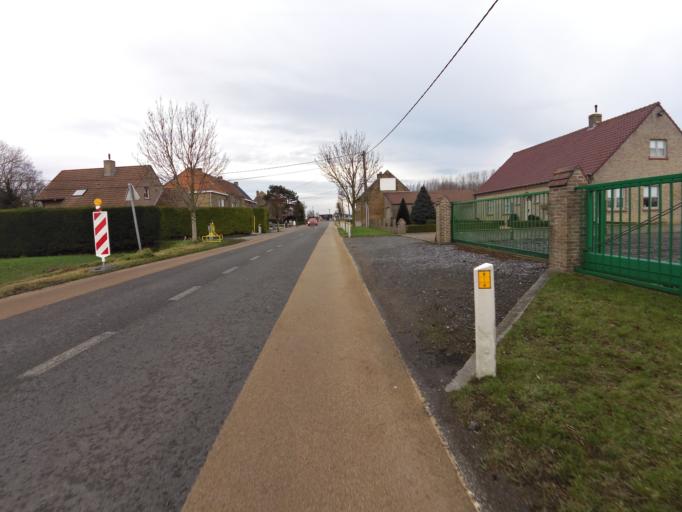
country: BE
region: Flanders
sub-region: Provincie West-Vlaanderen
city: Ostend
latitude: 51.1818
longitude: 2.8834
